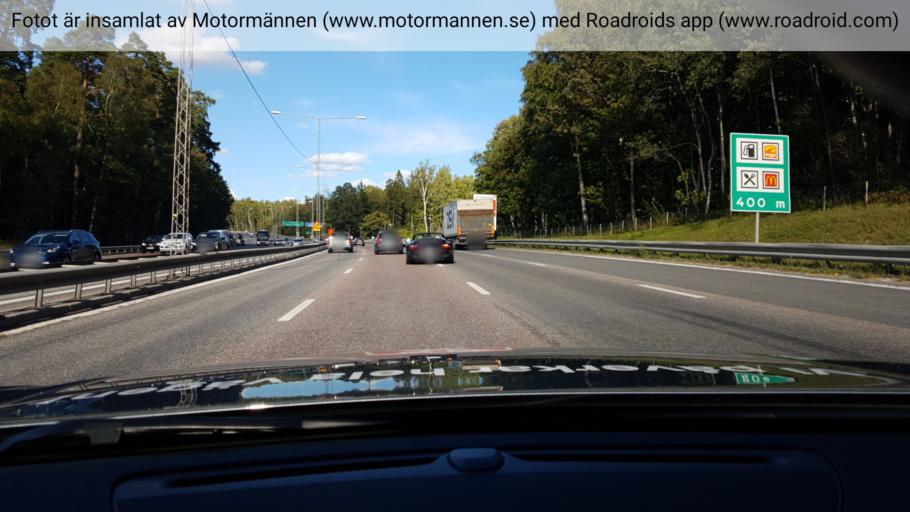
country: SE
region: Stockholm
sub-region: Botkyrka Kommun
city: Fittja
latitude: 59.2547
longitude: 17.8827
